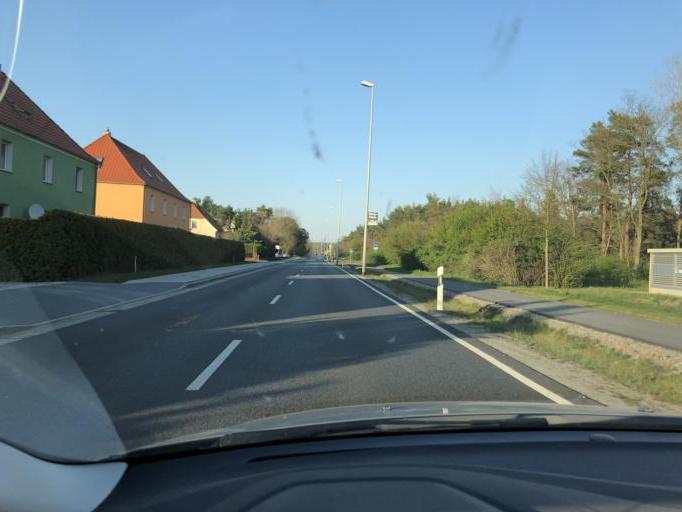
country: DE
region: Brandenburg
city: Ruhland
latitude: 51.4728
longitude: 13.8944
